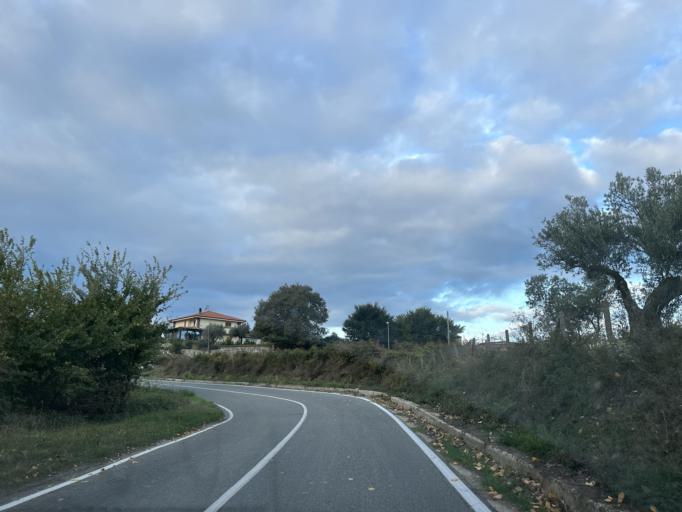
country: IT
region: Calabria
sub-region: Provincia di Catanzaro
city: Montauro
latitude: 38.7617
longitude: 16.5149
